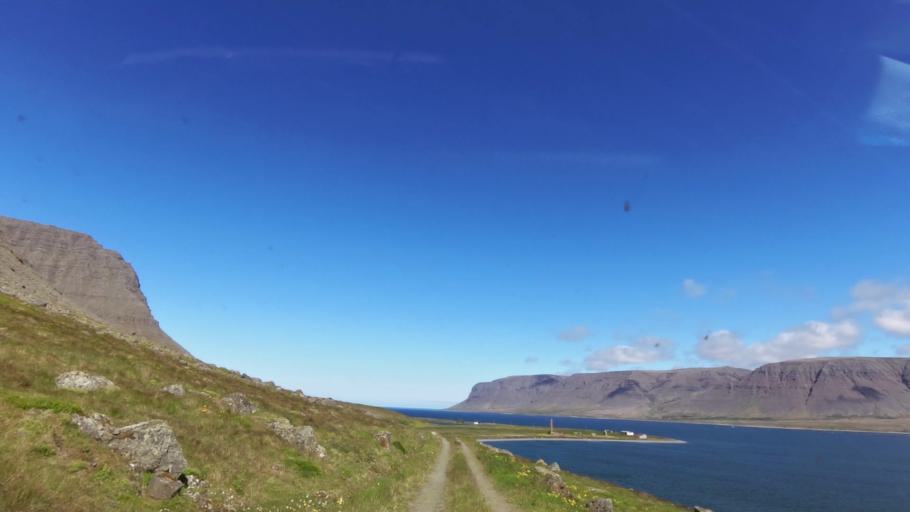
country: IS
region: West
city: Olafsvik
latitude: 65.6347
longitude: -23.9255
